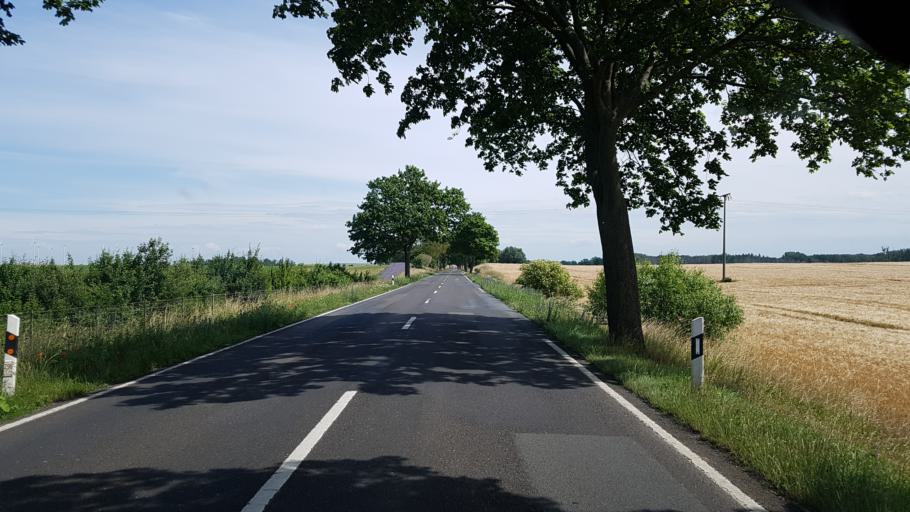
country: DE
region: Mecklenburg-Vorpommern
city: Strasburg
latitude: 53.3995
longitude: 13.7557
